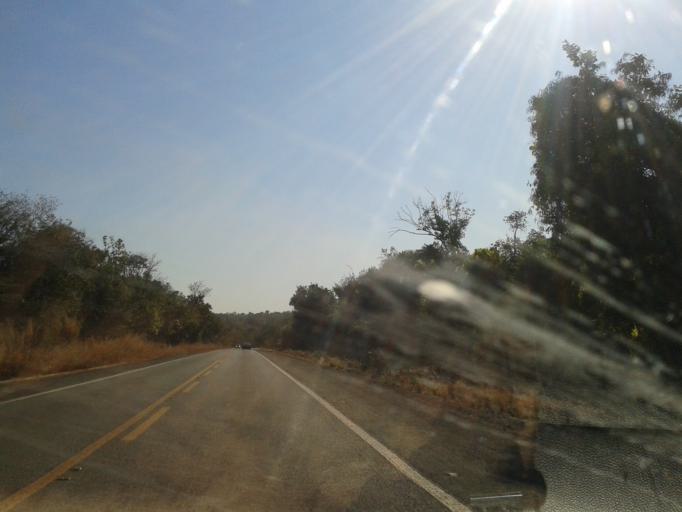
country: BR
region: Goias
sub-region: Mozarlandia
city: Mozarlandia
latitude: -14.8364
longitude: -50.5389
